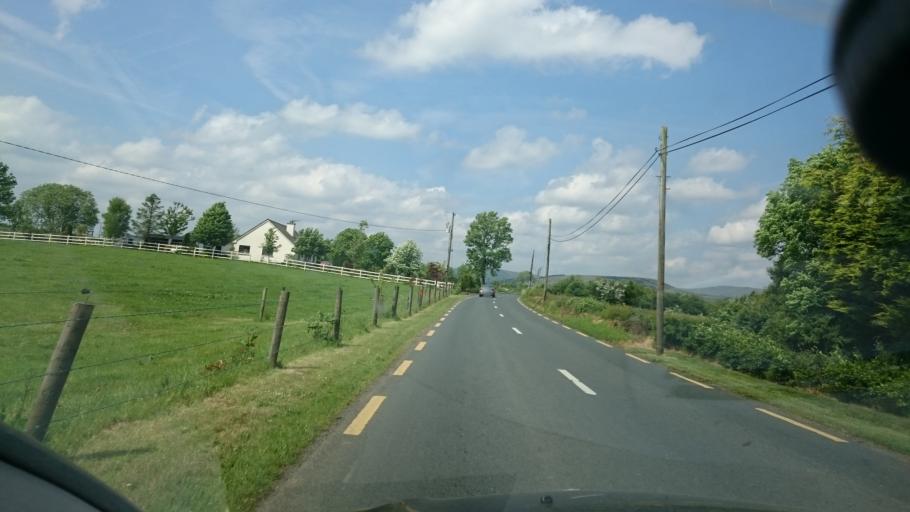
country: IE
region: Connaught
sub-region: Sligo
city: Tobercurry
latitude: 54.0579
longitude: -8.8182
